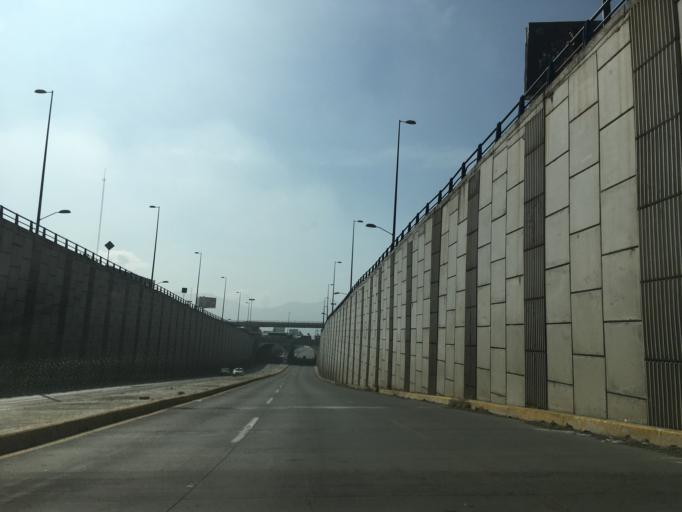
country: MX
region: Michoacan
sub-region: Morelia
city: San Antonio
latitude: 19.7028
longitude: -101.2446
